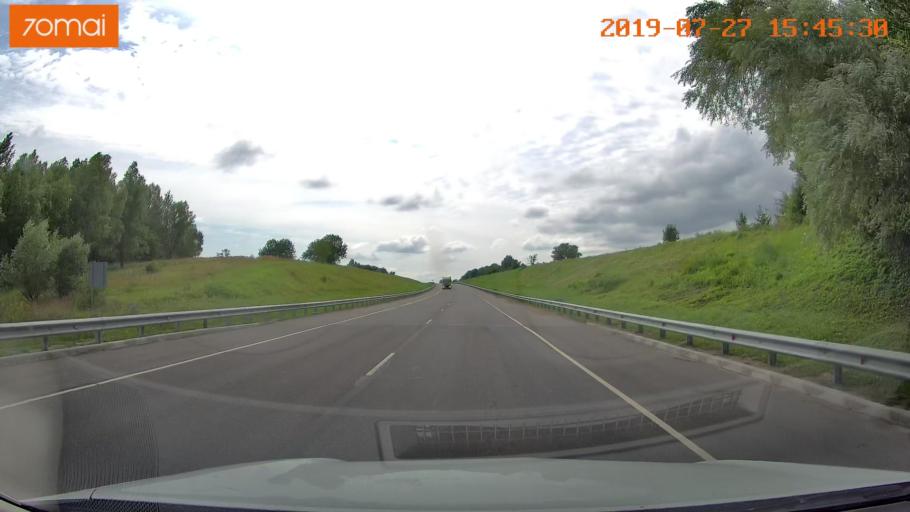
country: RU
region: Kaliningrad
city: Gusev
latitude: 54.6114
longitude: 22.1368
